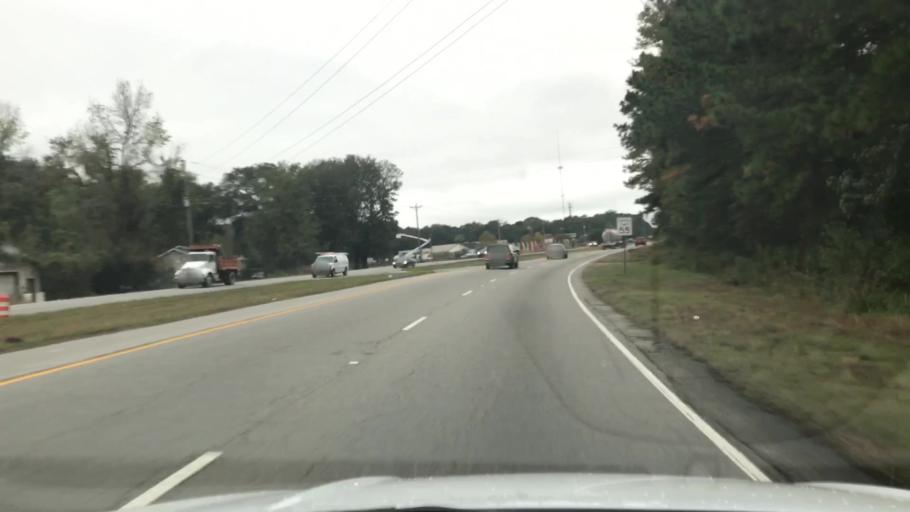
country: US
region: South Carolina
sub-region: Charleston County
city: Shell Point
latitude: 32.7817
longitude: -80.1516
